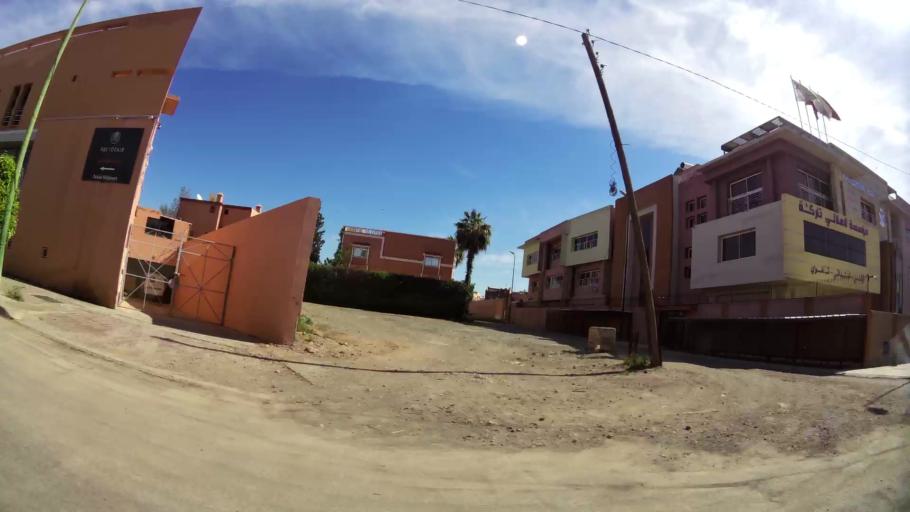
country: MA
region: Marrakech-Tensift-Al Haouz
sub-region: Marrakech
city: Marrakesh
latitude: 31.6584
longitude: -8.0566
